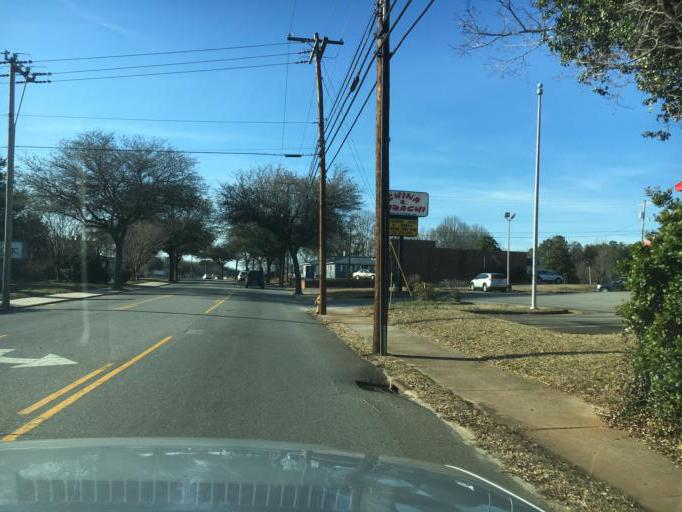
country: US
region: North Carolina
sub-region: Rutherford County
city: Forest City
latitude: 35.3390
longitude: -81.8745
